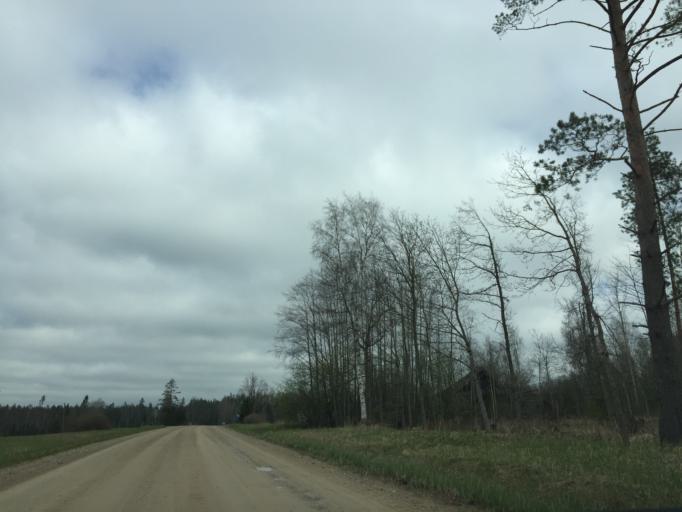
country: EE
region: Valgamaa
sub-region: Valga linn
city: Valga
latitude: 57.6047
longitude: 26.2280
